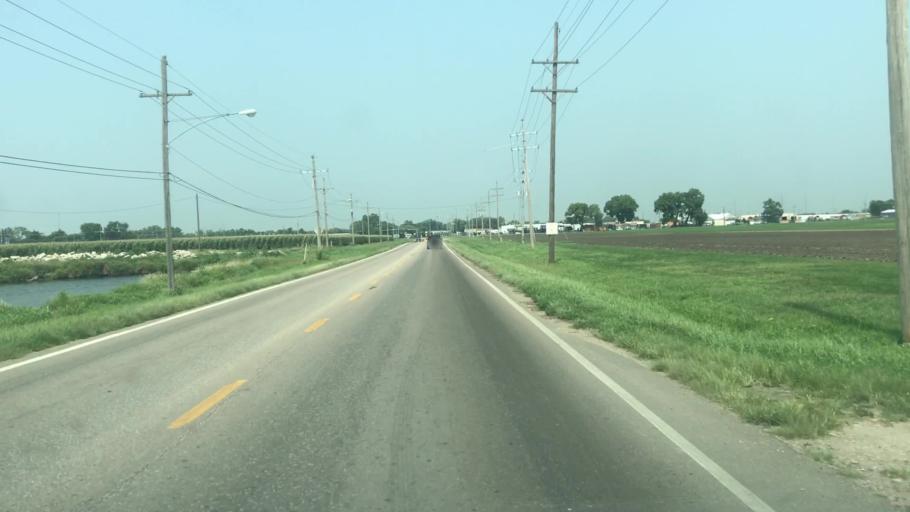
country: US
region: Nebraska
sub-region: Hall County
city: Grand Island
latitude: 40.9264
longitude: -98.3206
